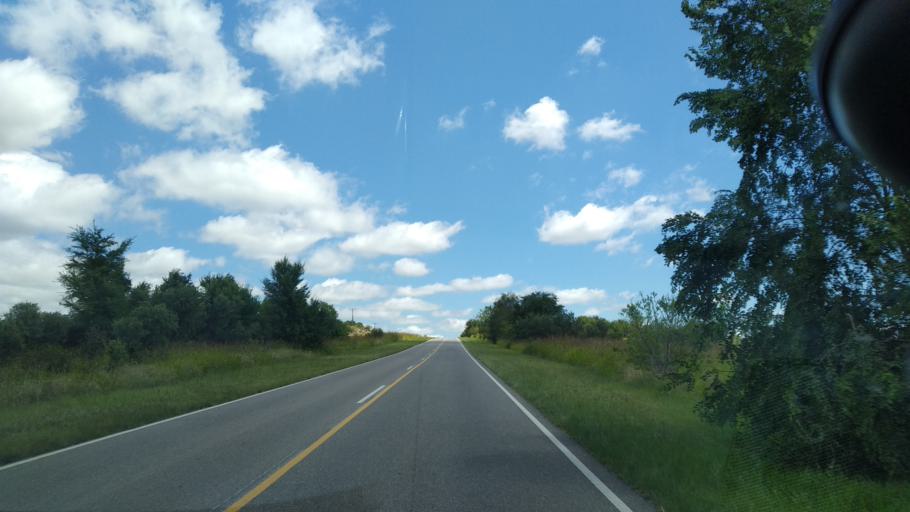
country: AR
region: Cordoba
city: Villa Cura Brochero
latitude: -31.6312
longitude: -65.1059
